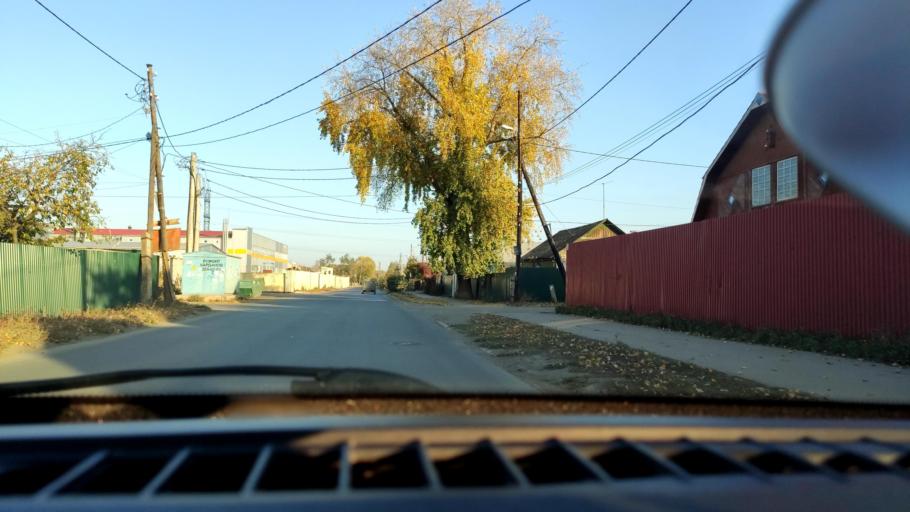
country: RU
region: Samara
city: Samara
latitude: 53.1844
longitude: 50.2337
